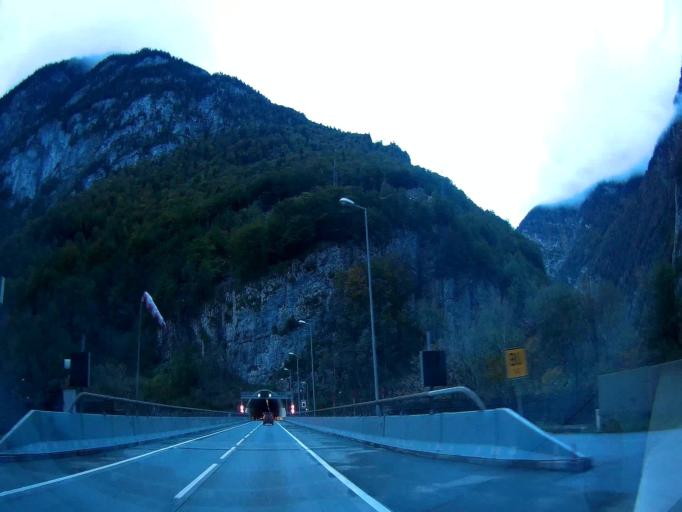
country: AT
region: Salzburg
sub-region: Politischer Bezirk Hallein
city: Golling an der Salzach
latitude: 47.5718
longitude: 13.1662
